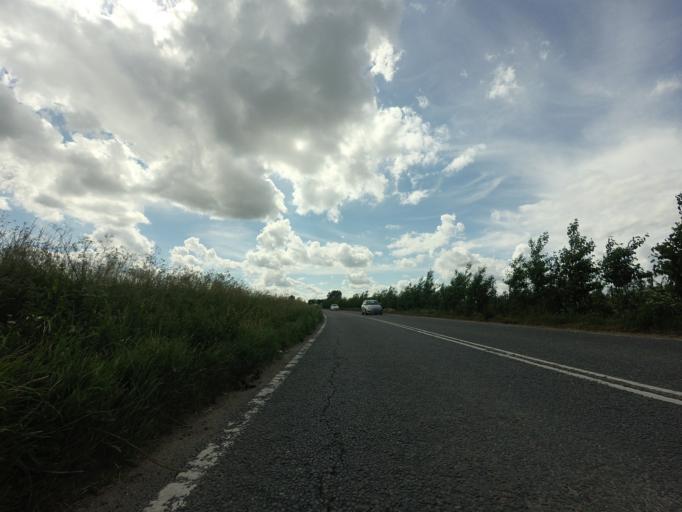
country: GB
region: England
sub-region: Medway
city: Stoke
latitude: 51.4489
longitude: 0.6060
